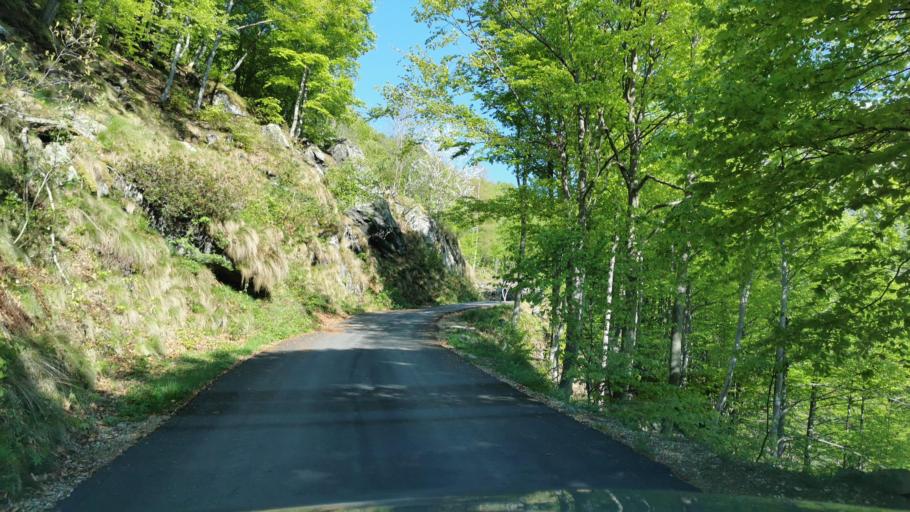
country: IT
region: Piedmont
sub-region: Provincia di Torino
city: Lemie
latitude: 45.2393
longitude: 7.2830
